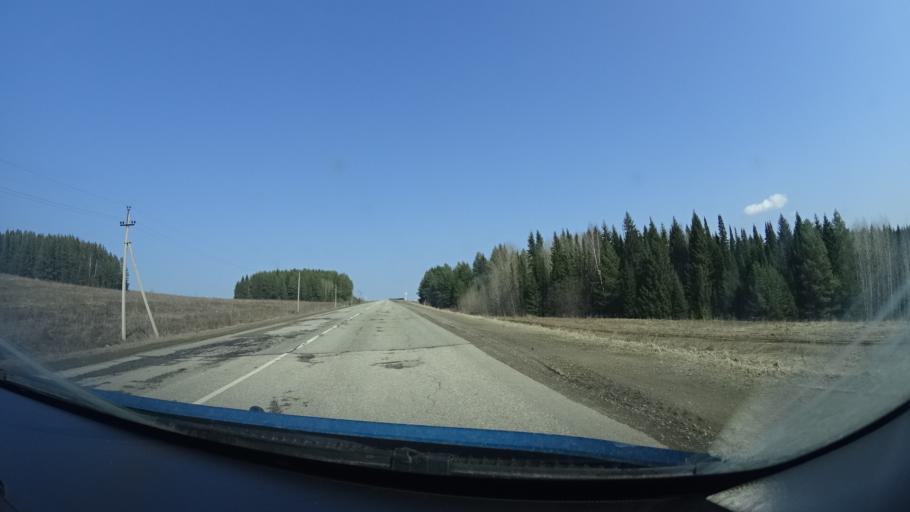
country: RU
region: Perm
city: Osa
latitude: 57.3111
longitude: 55.6203
